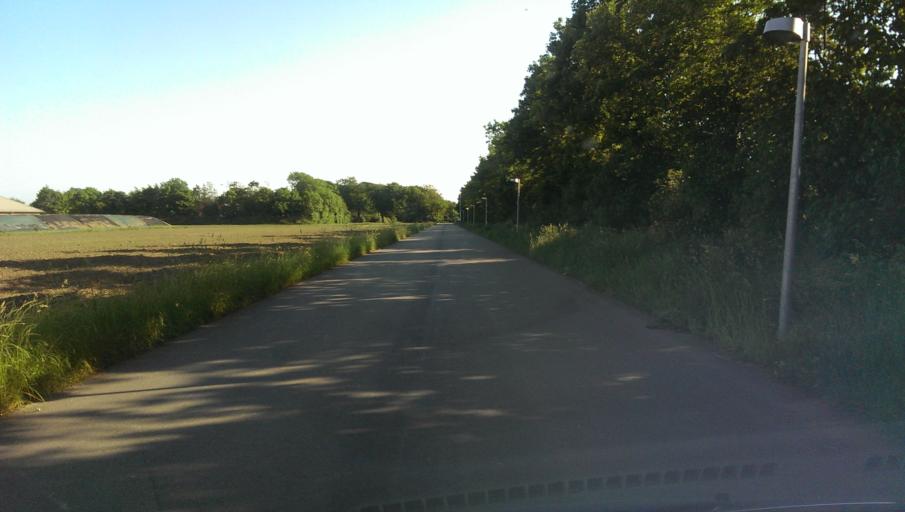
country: DK
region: South Denmark
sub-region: Esbjerg Kommune
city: Bramming
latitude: 55.5257
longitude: 8.7018
